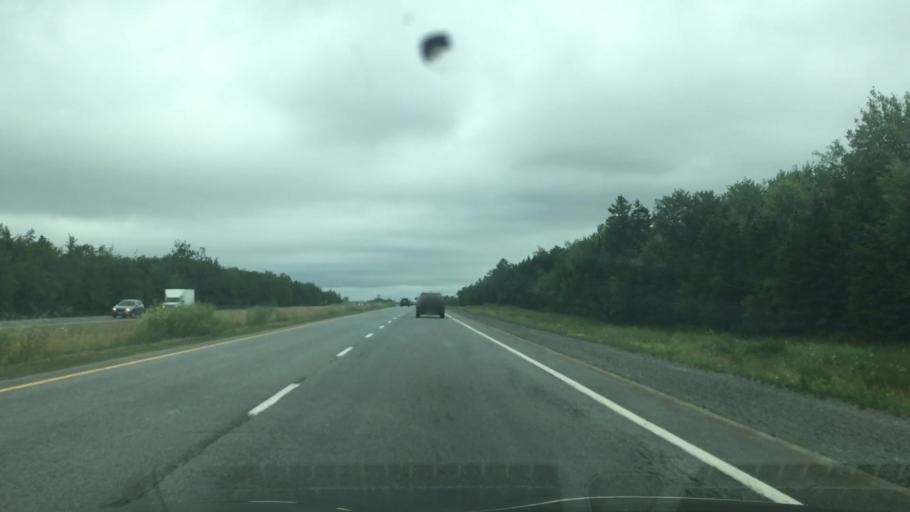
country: CA
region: Nova Scotia
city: Cole Harbour
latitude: 44.9905
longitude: -63.4964
